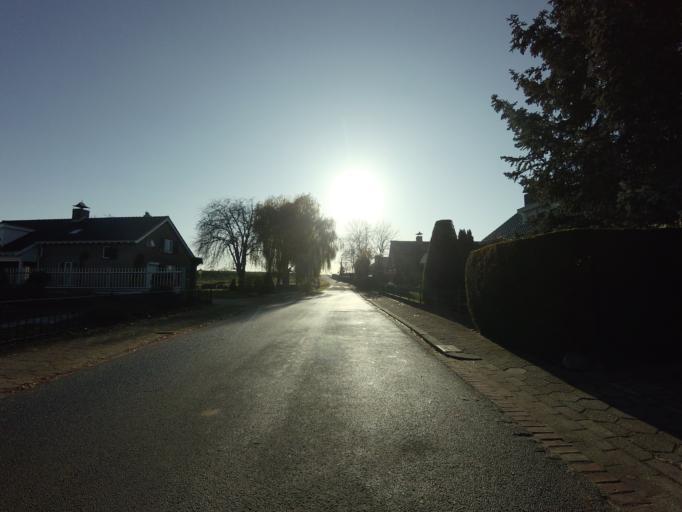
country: NL
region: Gelderland
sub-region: Gemeente Maasdriel
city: Heerewaarden
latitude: 51.7630
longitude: 5.3428
